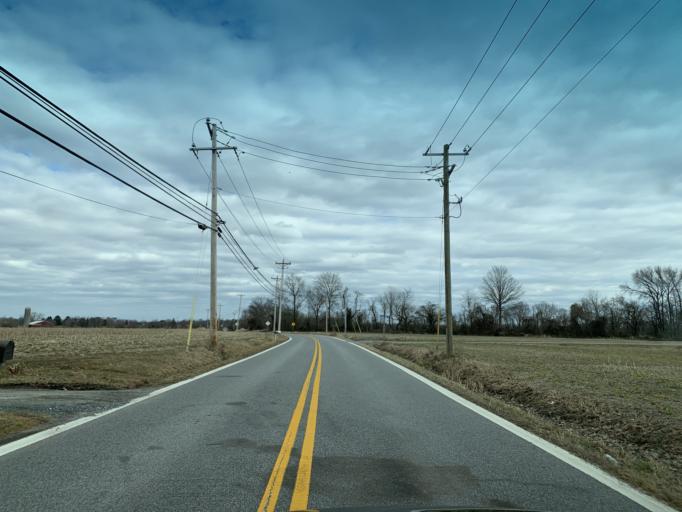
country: US
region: Maryland
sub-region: Queen Anne's County
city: Centreville
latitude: 39.0299
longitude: -76.0929
